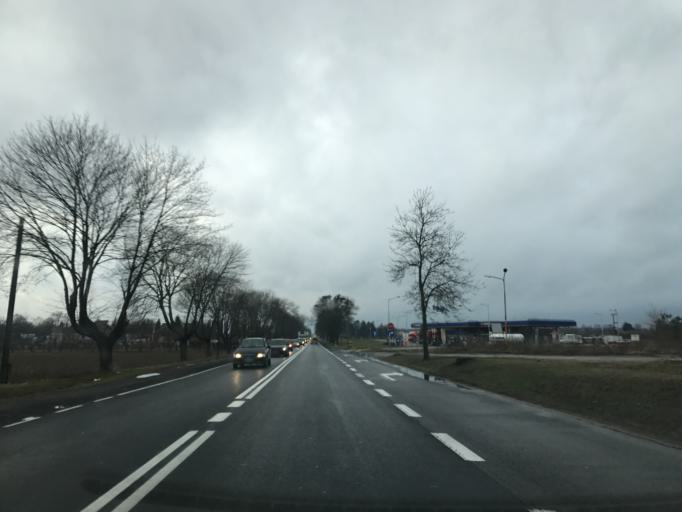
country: PL
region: Lodz Voivodeship
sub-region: Piotrkow Trybunalski
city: Piotrkow Trybunalski
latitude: 51.3900
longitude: 19.7770
